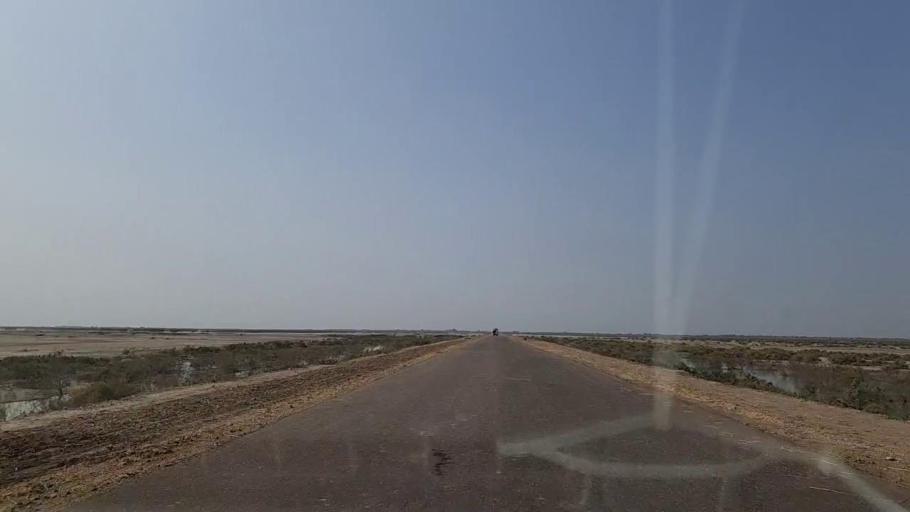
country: PK
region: Sindh
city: Chuhar Jamali
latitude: 24.2226
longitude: 67.8920
